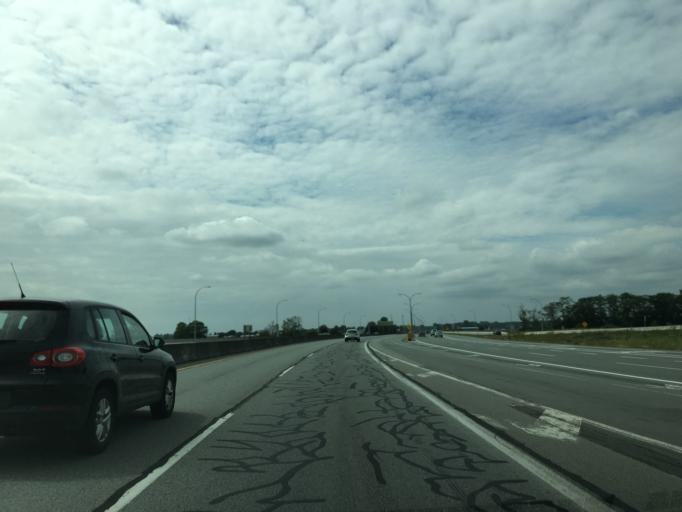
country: CA
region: British Columbia
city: Ladner
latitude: 49.0959
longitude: -123.0288
